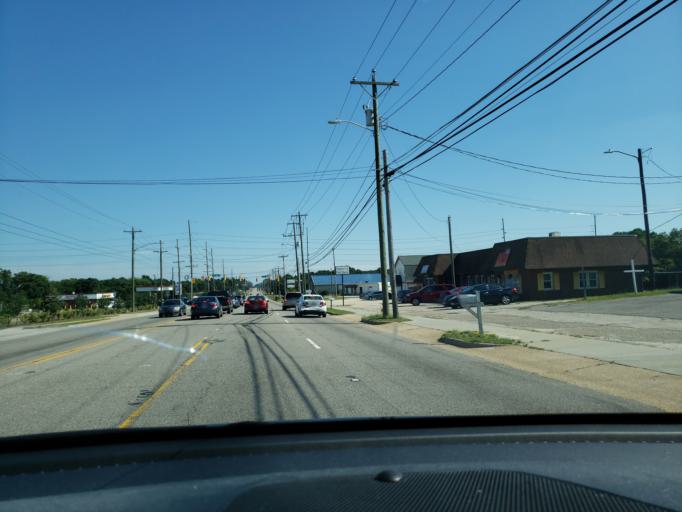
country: US
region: North Carolina
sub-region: Cumberland County
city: Spring Lake
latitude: 35.1125
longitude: -78.9286
